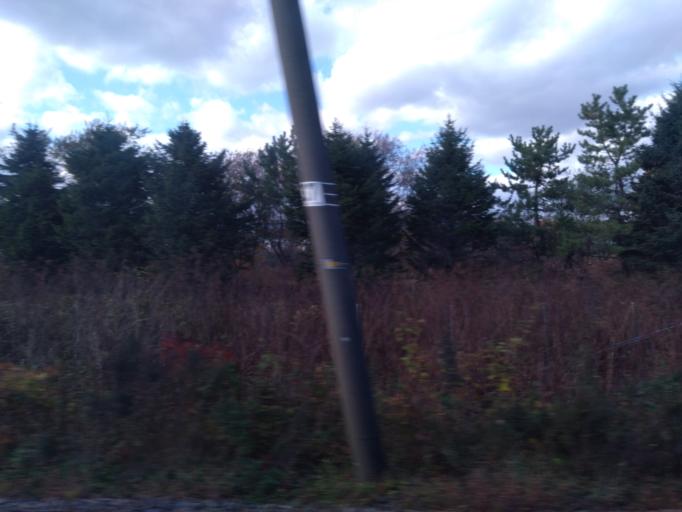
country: JP
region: Hokkaido
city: Shiraoi
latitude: 42.5063
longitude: 141.2818
